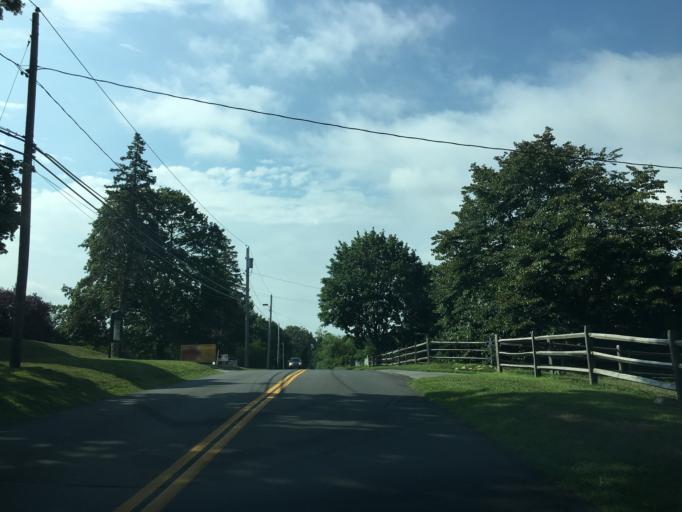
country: US
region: New York
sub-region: Suffolk County
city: Shelter Island
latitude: 41.0730
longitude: -72.3322
